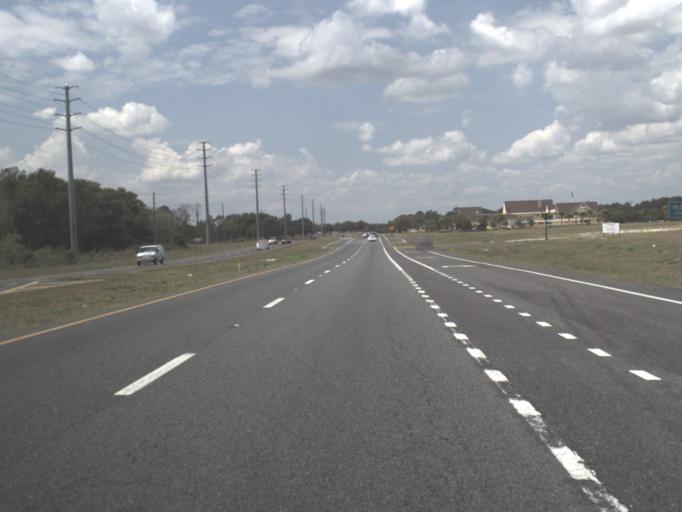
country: US
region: Florida
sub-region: Lake County
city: Fruitland Park
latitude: 28.8231
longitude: -81.9666
